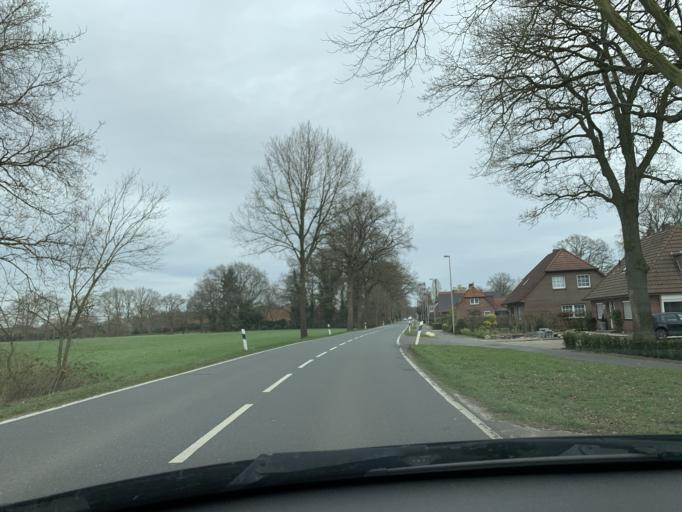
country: DE
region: Lower Saxony
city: Bad Zwischenahn
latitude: 53.1741
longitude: 7.9671
